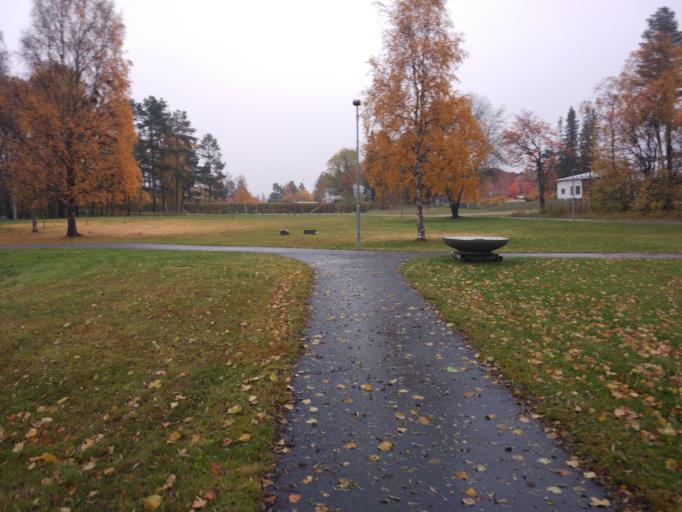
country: SE
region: Vaesterbotten
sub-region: Umea Kommun
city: Holmsund
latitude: 63.7036
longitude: 20.3707
